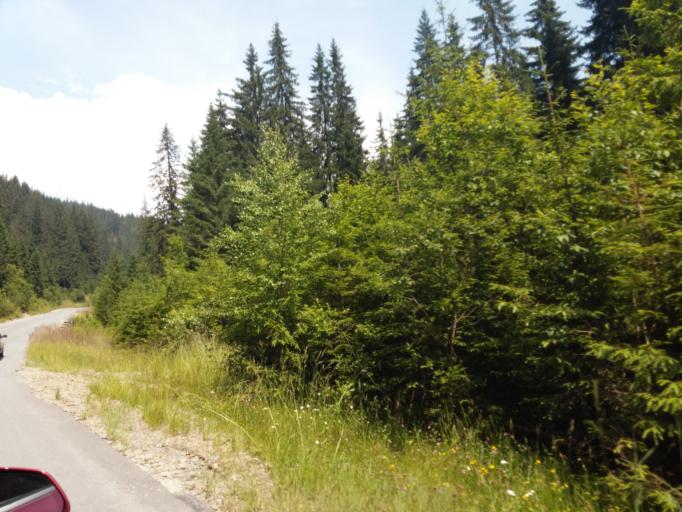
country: RO
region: Valcea
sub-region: Comuna Voineasa
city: Voineasa
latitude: 45.4246
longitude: 23.7801
